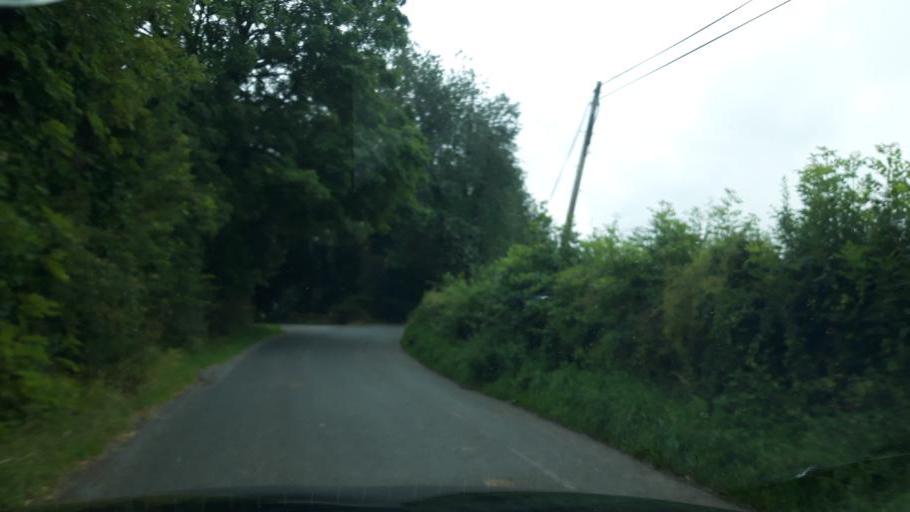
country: IE
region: Leinster
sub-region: Kilkenny
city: Ballyragget
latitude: 52.7097
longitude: -7.4023
